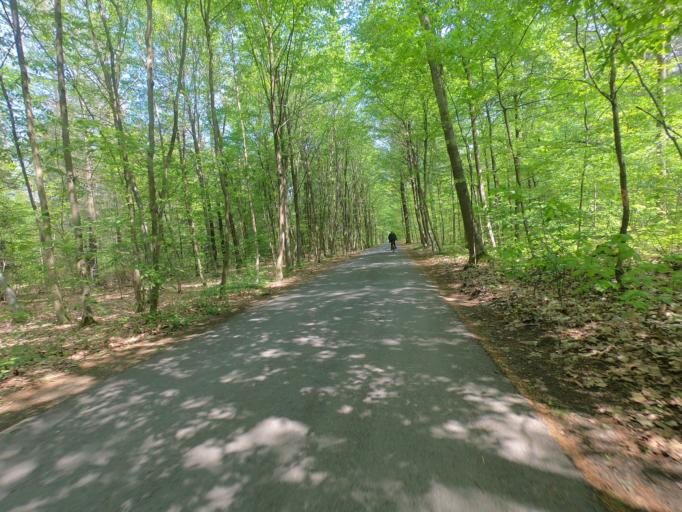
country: DE
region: Hesse
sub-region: Regierungsbezirk Darmstadt
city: Neu Isenburg
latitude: 50.0662
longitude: 8.6729
